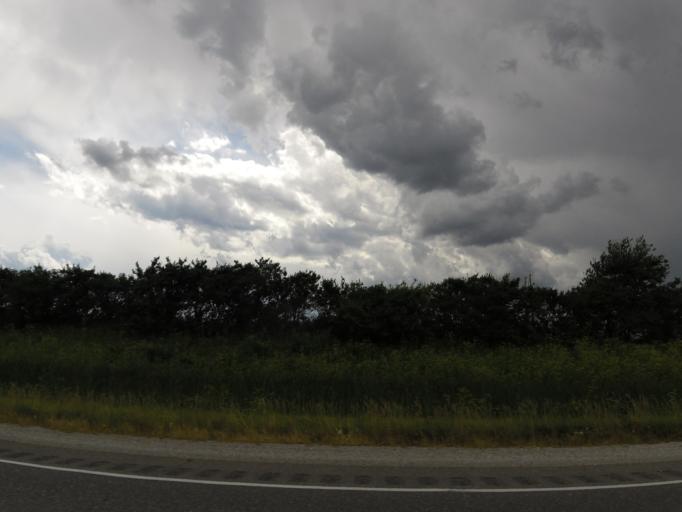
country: US
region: Iowa
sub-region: Johnson County
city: Lone Tree
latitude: 41.4089
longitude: -91.5504
